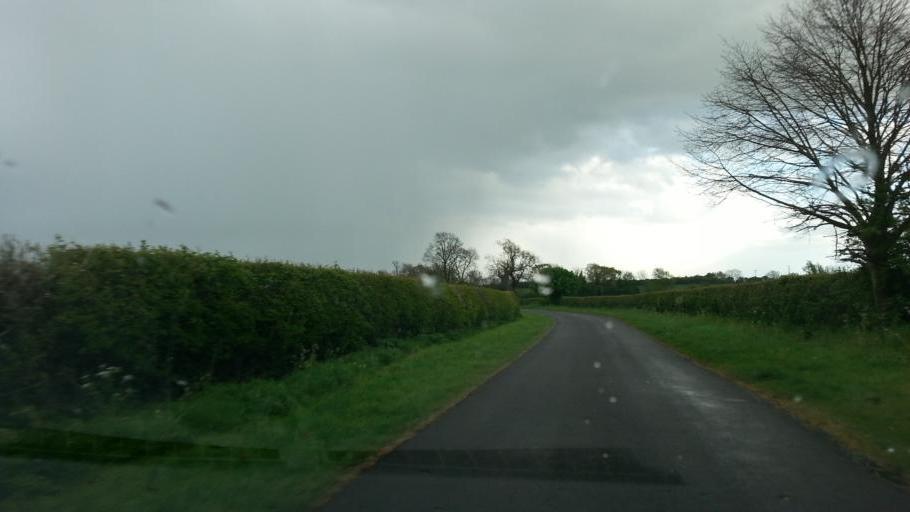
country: GB
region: England
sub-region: Nottinghamshire
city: Farndon
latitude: 52.9801
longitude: -0.8814
